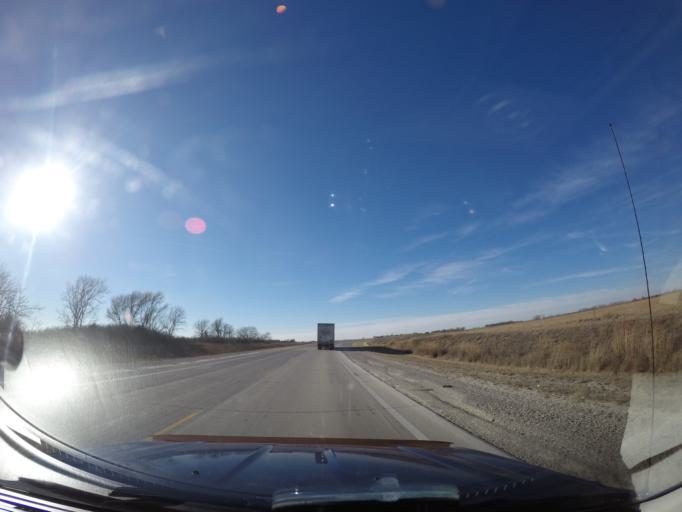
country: US
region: Kansas
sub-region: Marion County
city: Marion
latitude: 38.3558
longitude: -97.0987
